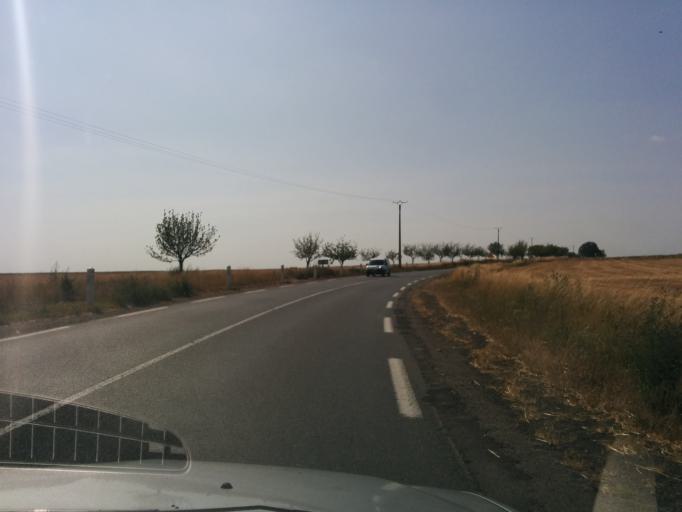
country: FR
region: Poitou-Charentes
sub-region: Departement de la Vienne
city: Neuville-de-Poitou
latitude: 46.7139
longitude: 0.2147
